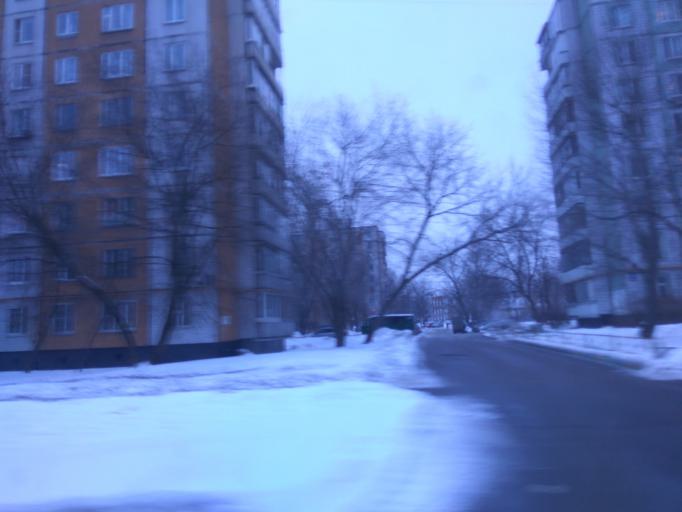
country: RU
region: Moscow
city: Gol'yanovo
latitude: 55.8156
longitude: 37.8279
